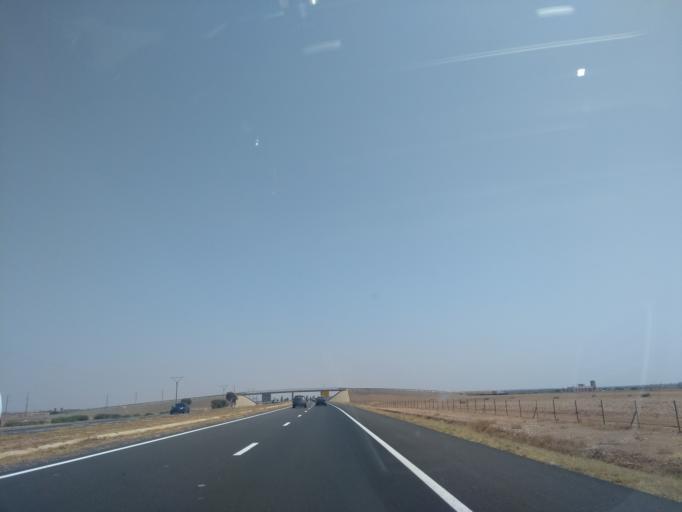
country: MA
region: Marrakech-Tensift-Al Haouz
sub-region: Kelaa-Des-Sraghna
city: Sidi Bou Othmane
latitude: 31.9330
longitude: -8.0181
